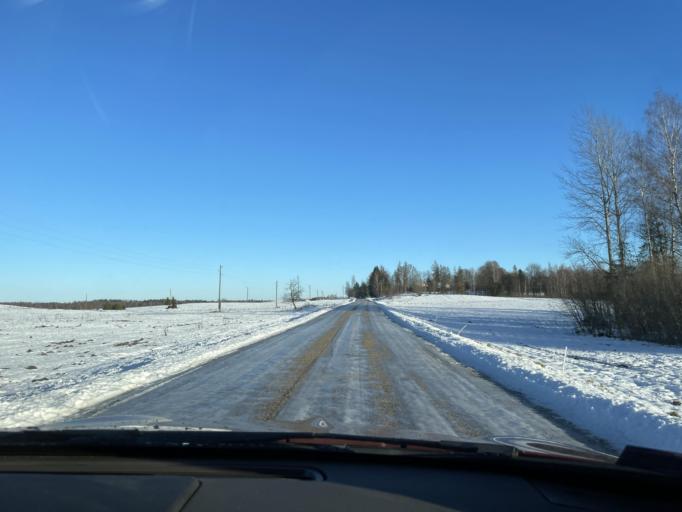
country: LV
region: Ludzas Rajons
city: Ludza
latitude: 56.4511
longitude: 27.5520
